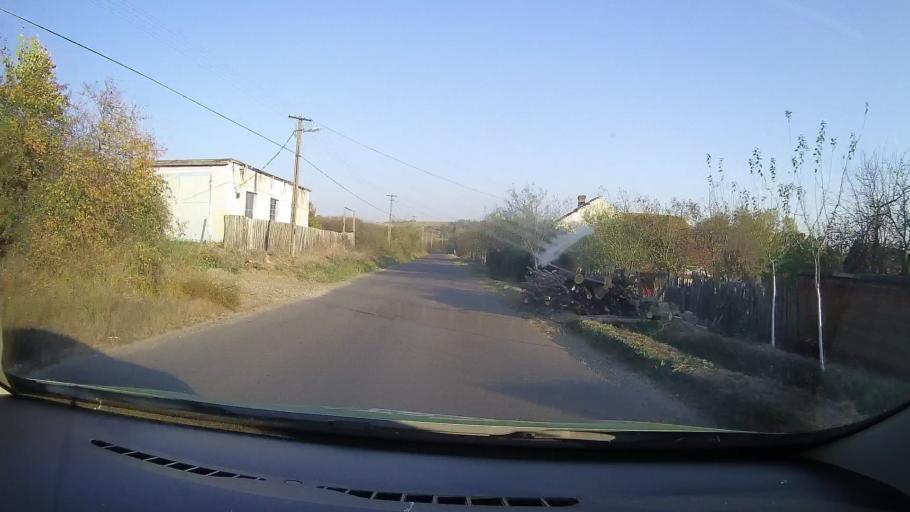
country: RO
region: Arad
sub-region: Comuna Silindia
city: Silindia
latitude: 46.3357
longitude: 21.9282
